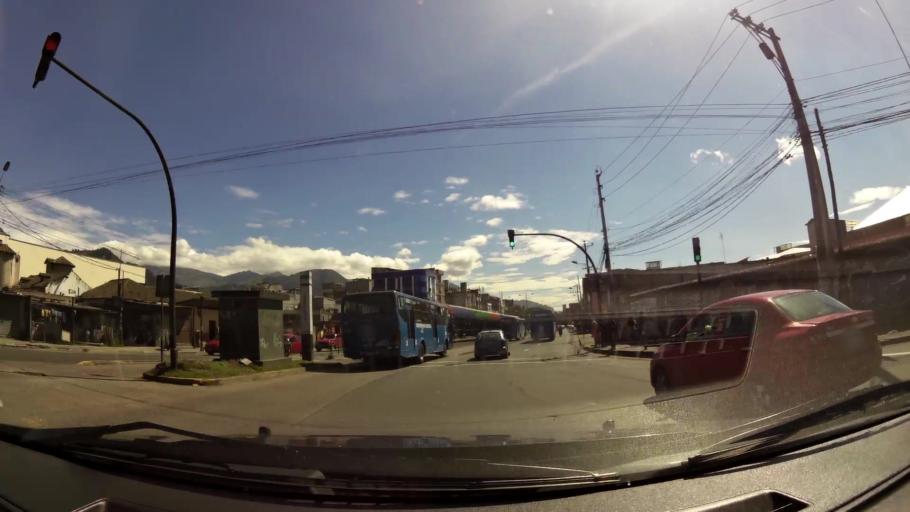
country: EC
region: Pichincha
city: Quito
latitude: -0.2827
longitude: -78.5543
